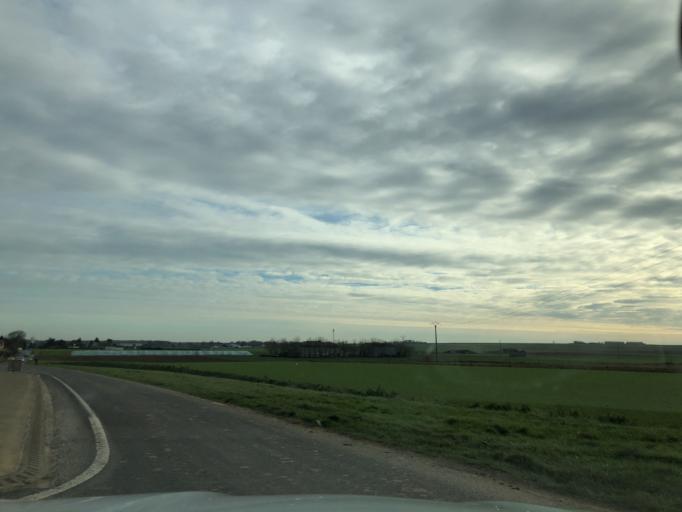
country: FR
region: Lower Normandy
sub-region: Departement du Calvados
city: Hermanville-sur-Mer
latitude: 49.2839
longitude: -0.3301
